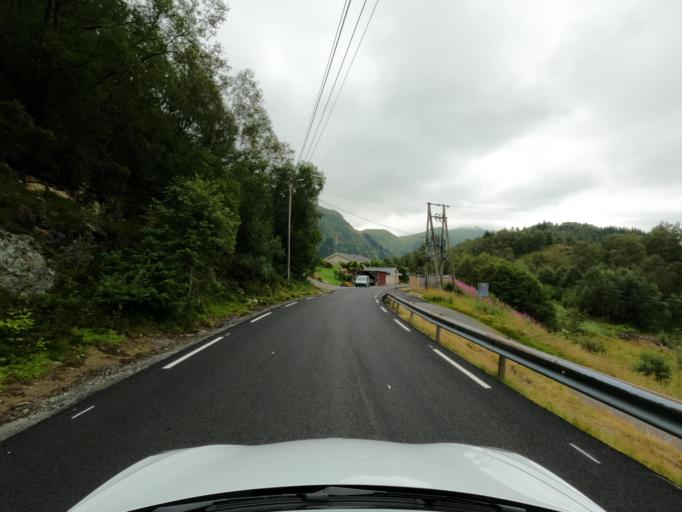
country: NO
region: Hordaland
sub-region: Bergen
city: Espeland
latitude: 60.3738
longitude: 5.4939
